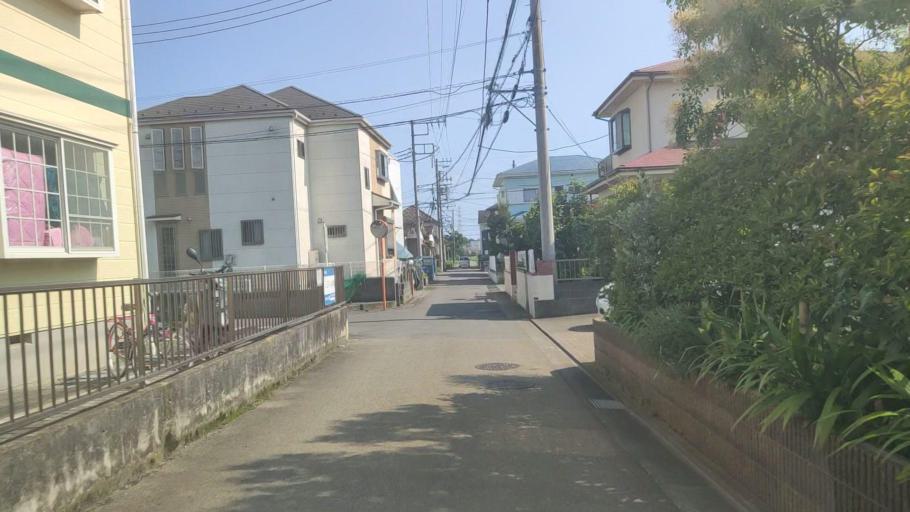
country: JP
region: Kanagawa
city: Hiratsuka
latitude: 35.3575
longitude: 139.3315
